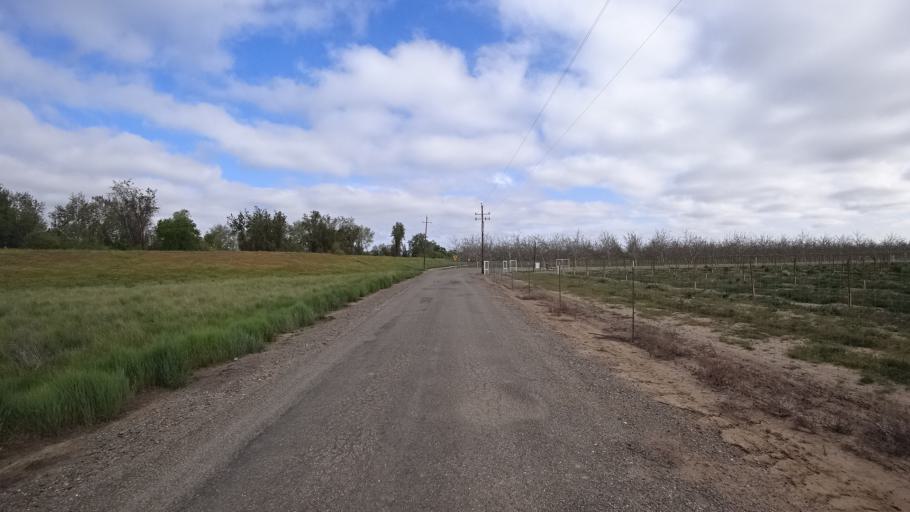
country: US
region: California
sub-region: Colusa County
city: Colusa
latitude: 39.4176
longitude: -121.9922
